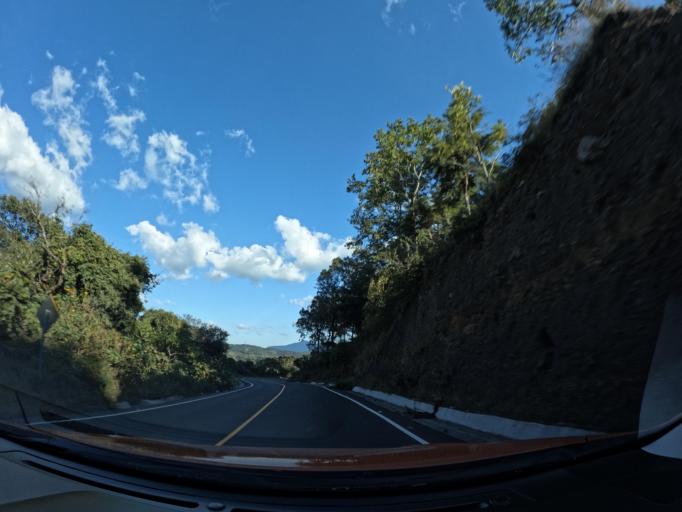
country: GT
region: Escuintla
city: Palin
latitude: 14.4520
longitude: -90.6937
